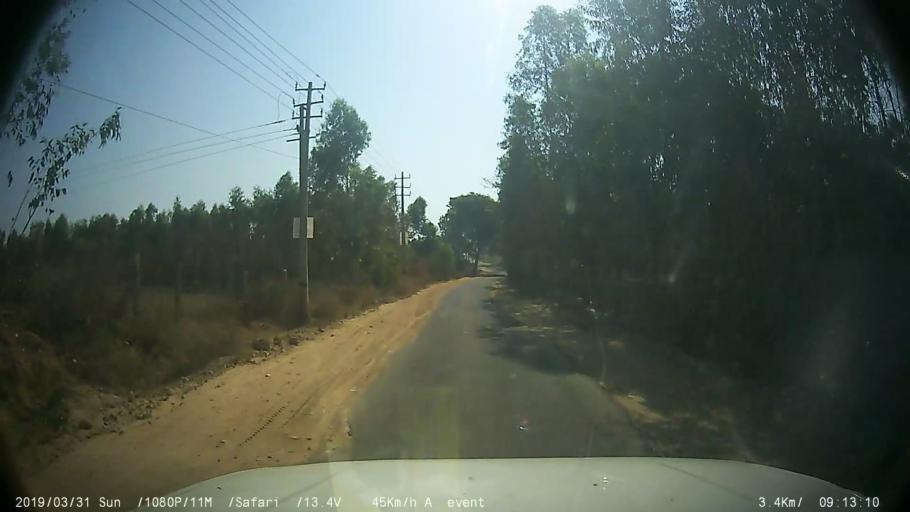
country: IN
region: Karnataka
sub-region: Bangalore Urban
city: Anekal
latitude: 12.8139
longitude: 77.6434
